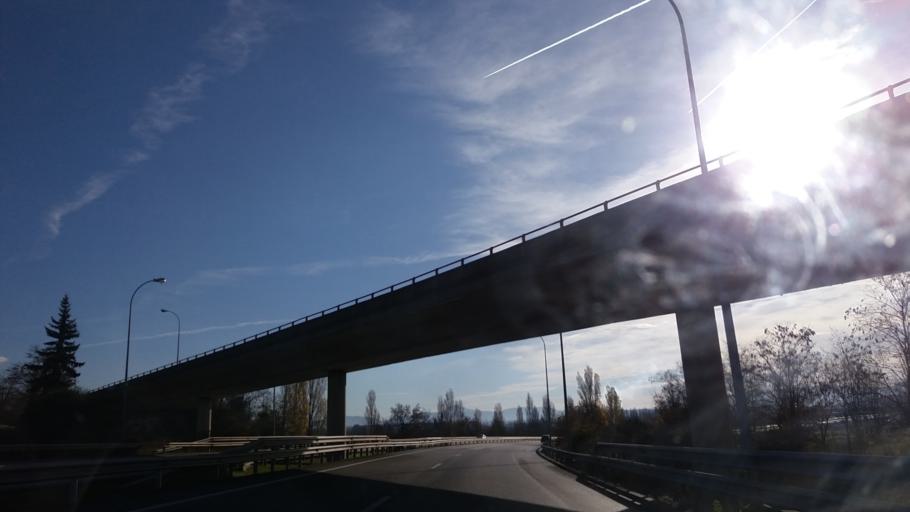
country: ES
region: Navarre
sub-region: Provincia de Navarra
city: Berriobeiti
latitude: 42.8443
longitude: -1.6934
